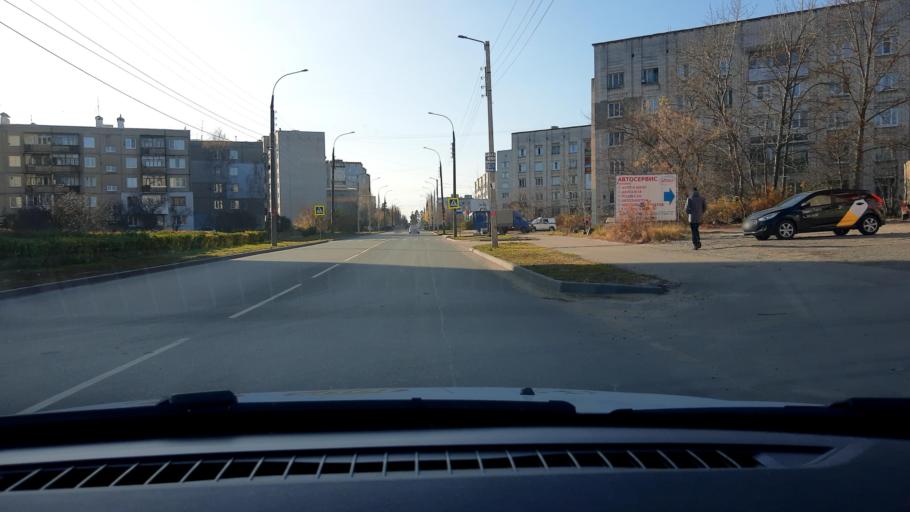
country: RU
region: Nizjnij Novgorod
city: Dzerzhinsk
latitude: 56.2560
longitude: 43.4532
